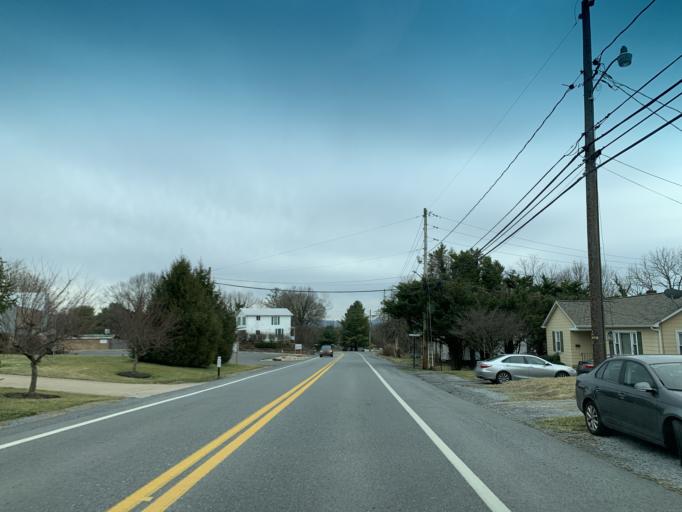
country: US
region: West Virginia
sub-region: Jefferson County
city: Charles Town
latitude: 39.2831
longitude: -77.8573
